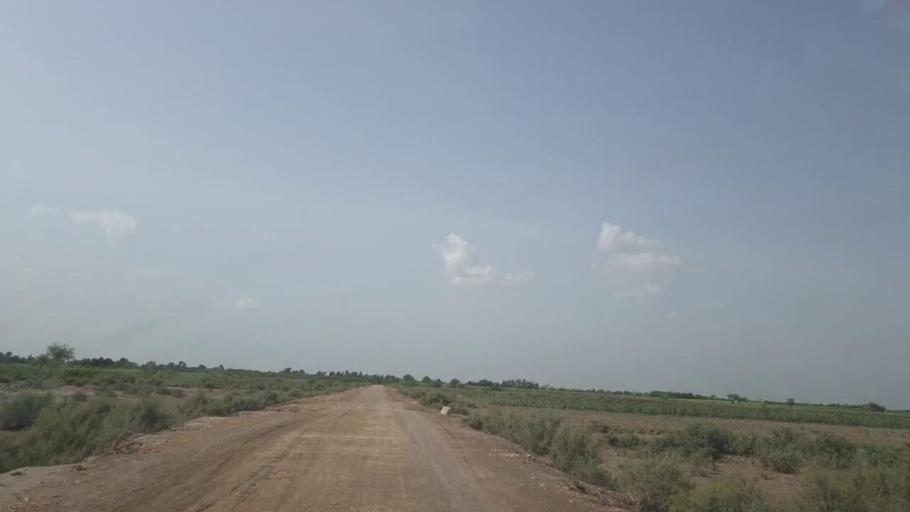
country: PK
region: Sindh
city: Tando Bago
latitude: 24.7742
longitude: 69.1305
